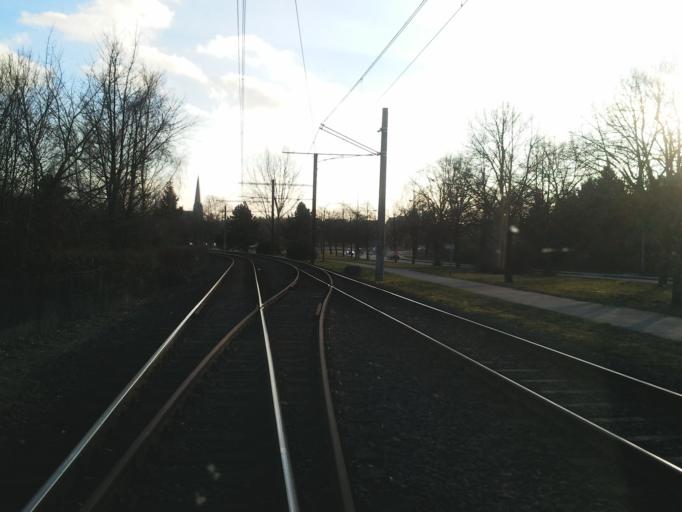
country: DE
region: Mecklenburg-Vorpommern
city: Dierkow-West
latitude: 54.1029
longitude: 12.1537
